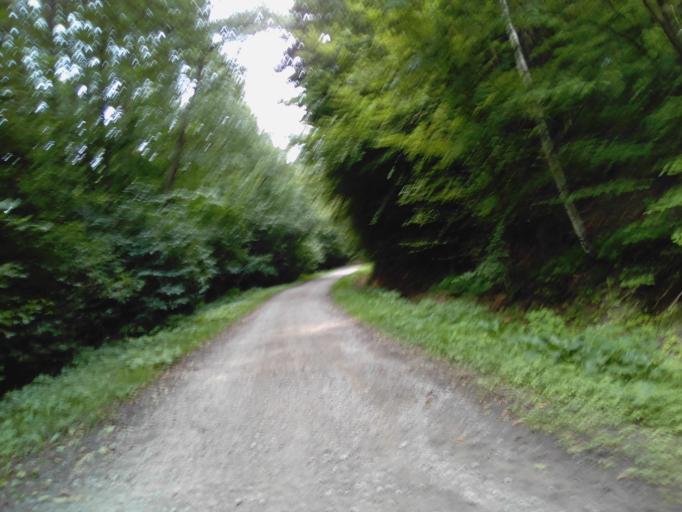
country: PL
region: Subcarpathian Voivodeship
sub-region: Powiat strzyzowski
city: Frysztak
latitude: 49.8787
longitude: 21.5552
